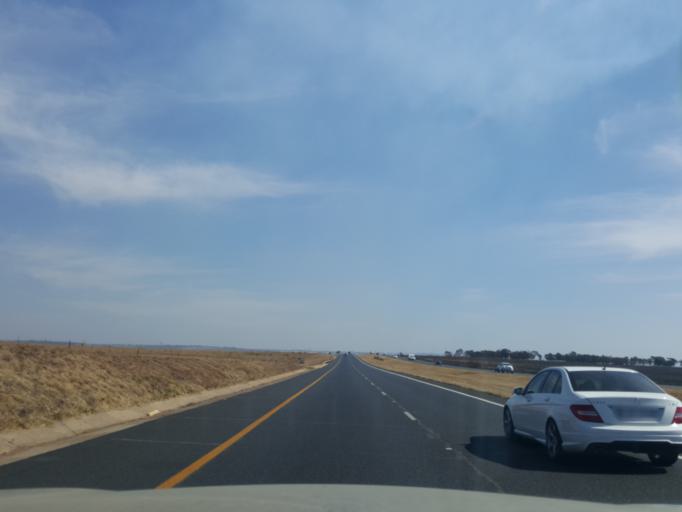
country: ZA
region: Mpumalanga
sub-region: Nkangala District Municipality
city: Witbank
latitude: -25.8768
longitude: 29.3425
